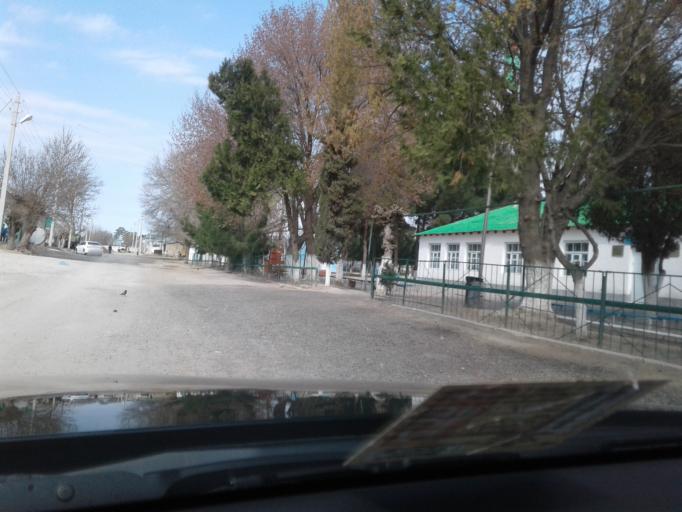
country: TM
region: Ahal
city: Abadan
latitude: 38.1205
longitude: 58.3494
